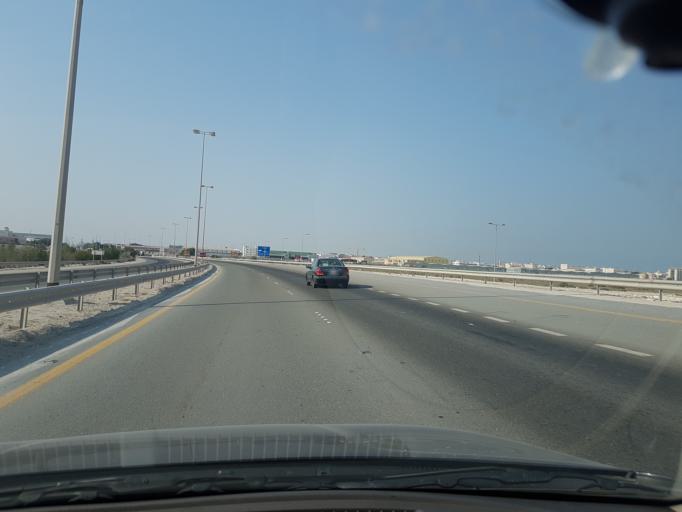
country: BH
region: Northern
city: Sitrah
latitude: 26.0701
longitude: 50.6152
